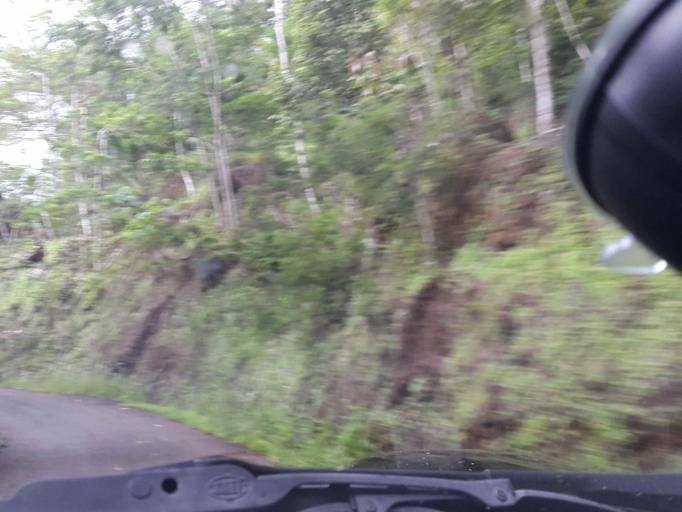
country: ID
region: Central Java
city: Wonosobo
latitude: -7.4831
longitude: 109.9062
